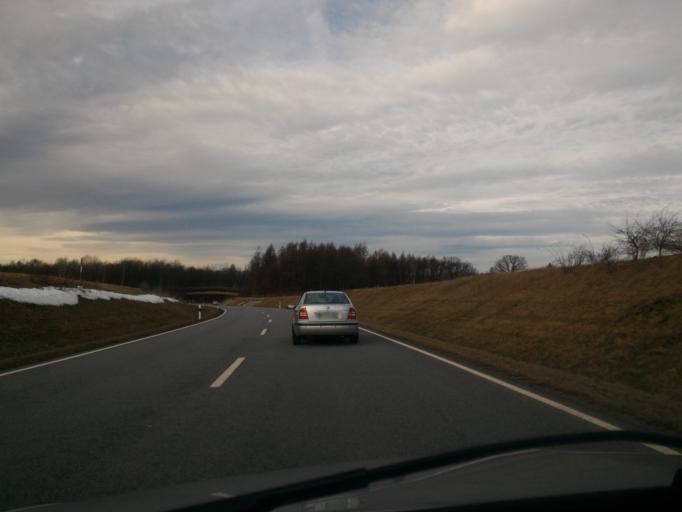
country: DE
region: Saxony
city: Bischofswerda
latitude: 51.1086
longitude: 14.1855
